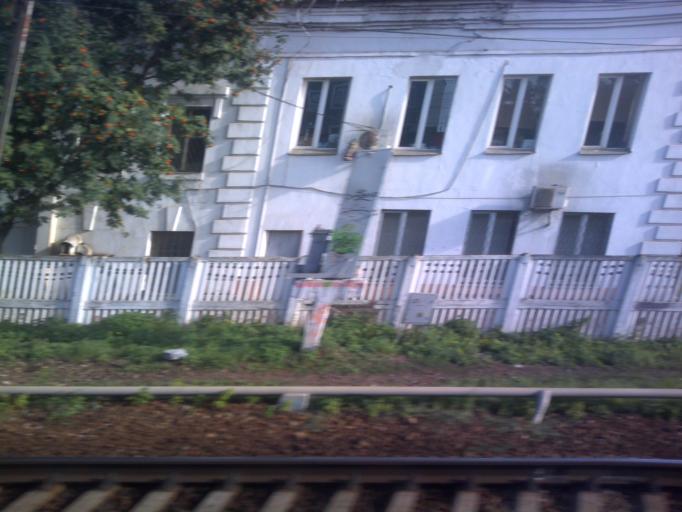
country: RU
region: Moscow
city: Zamoskvorech'ye
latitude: 55.7094
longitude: 37.6314
